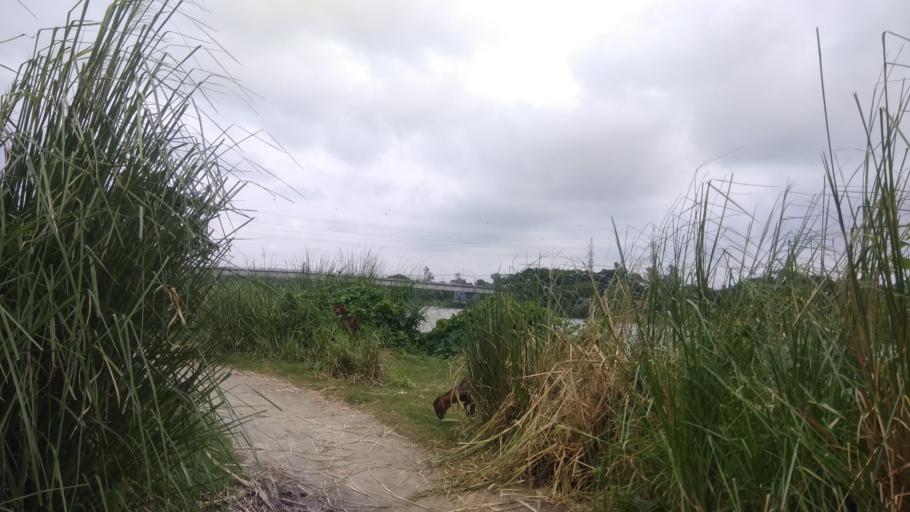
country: BD
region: Dhaka
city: Azimpur
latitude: 23.6722
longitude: 90.2869
